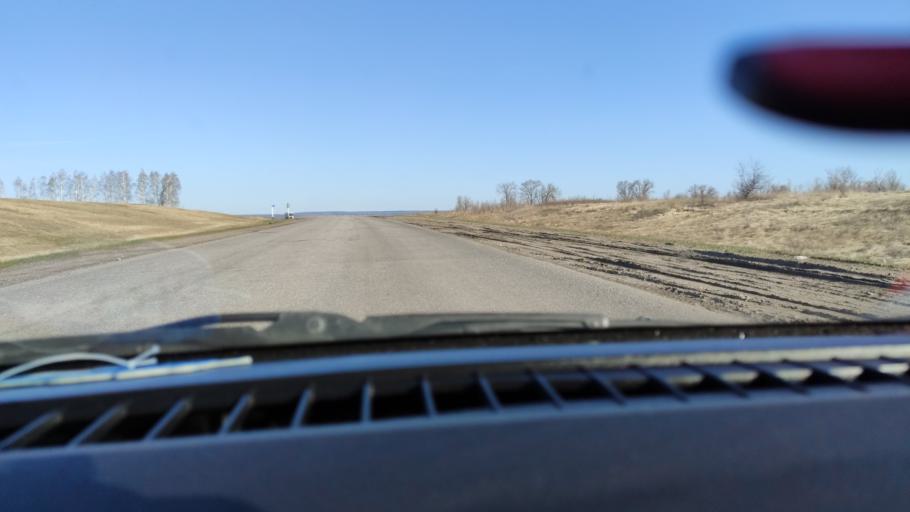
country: RU
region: Samara
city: Varlamovo
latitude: 53.1090
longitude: 48.3553
